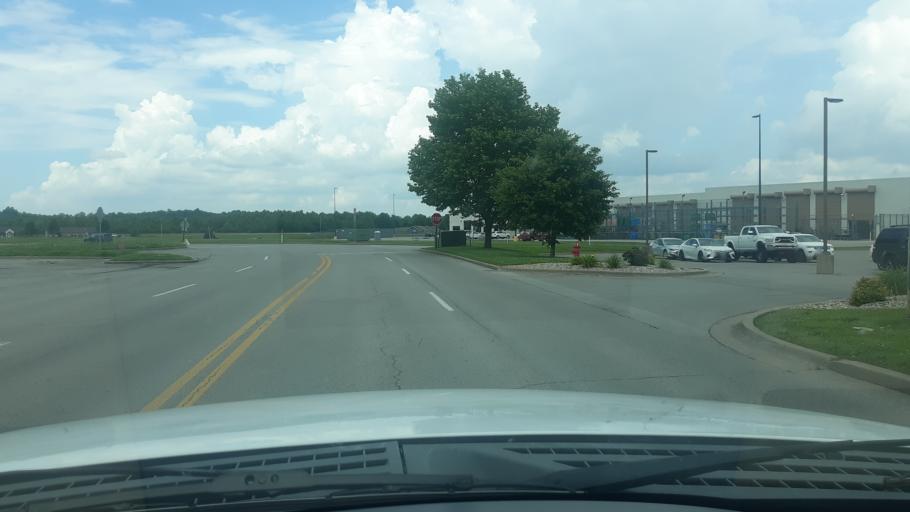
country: US
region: Illinois
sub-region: Williamson County
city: Marion
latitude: 37.7472
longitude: -88.9739
